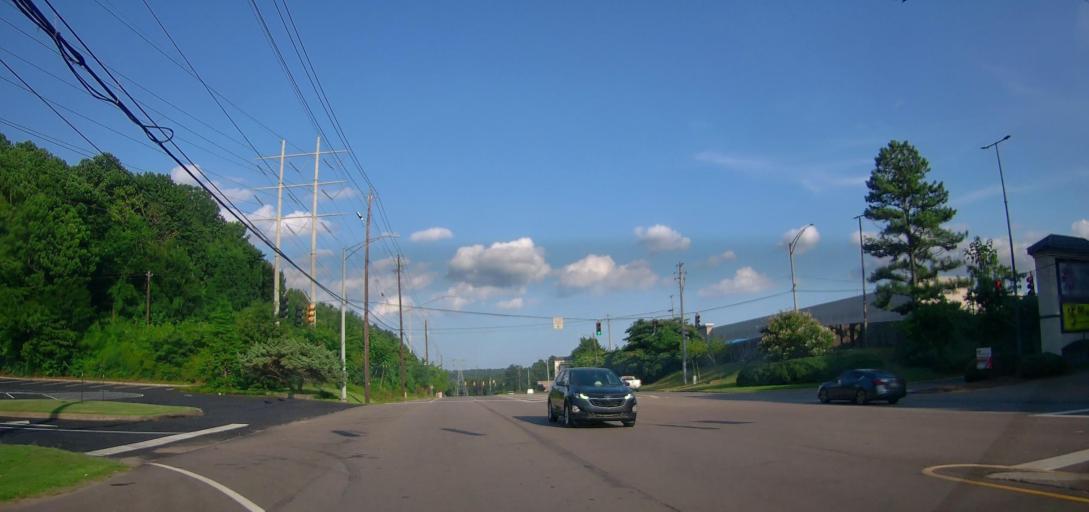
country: US
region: Alabama
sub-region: Jefferson County
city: Irondale
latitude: 33.5318
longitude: -86.7320
